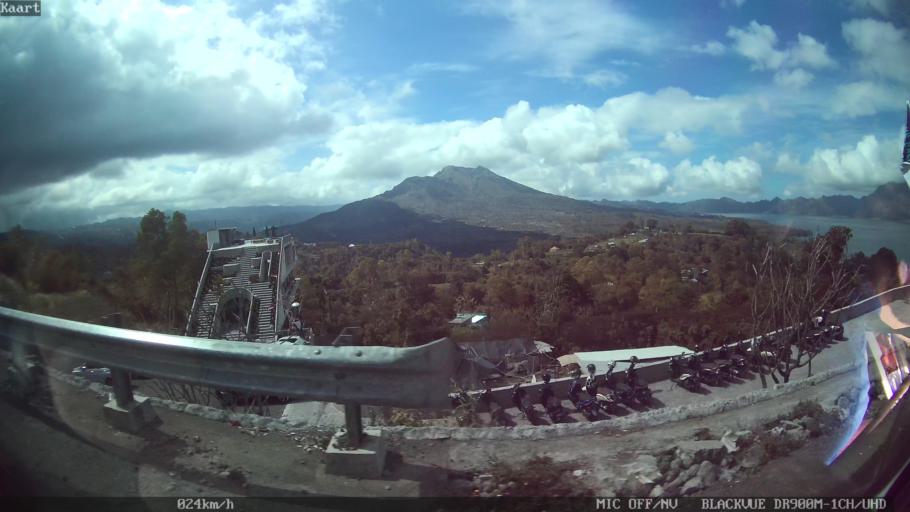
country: ID
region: Bali
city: Banjar Kedisan
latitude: -8.2800
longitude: 115.3695
